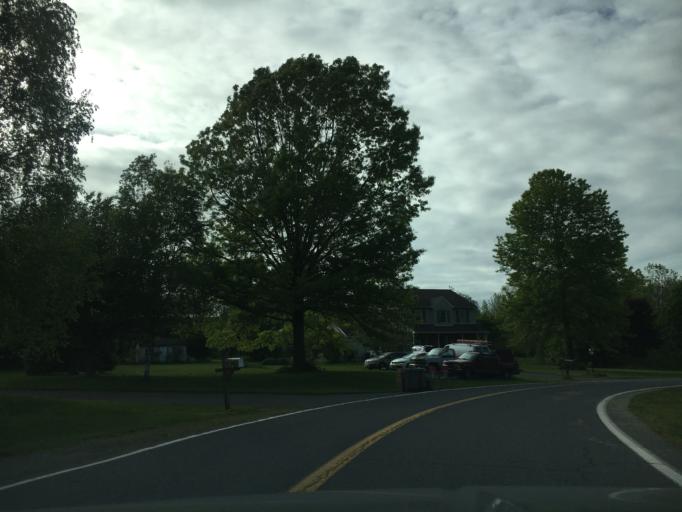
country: US
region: Pennsylvania
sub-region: Berks County
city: Fleetwood
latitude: 40.4515
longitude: -75.7748
